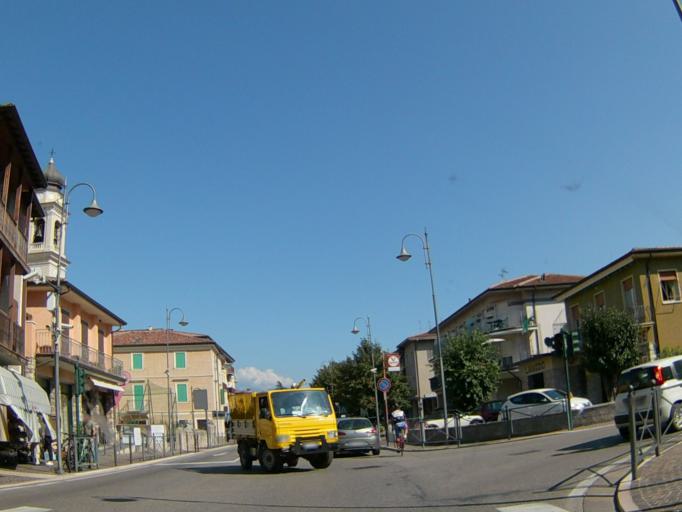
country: IT
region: Veneto
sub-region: Provincia di Verona
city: Torri del Benaco
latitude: 45.6099
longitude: 10.6870
